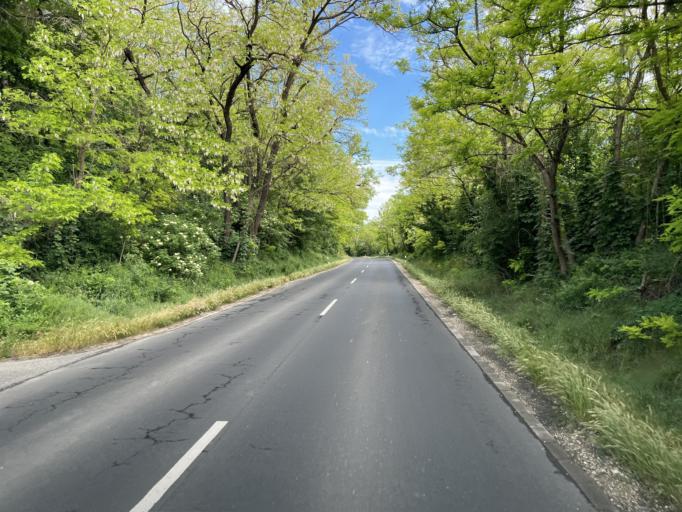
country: HU
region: Pest
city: Pecel
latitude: 47.5080
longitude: 19.3706
